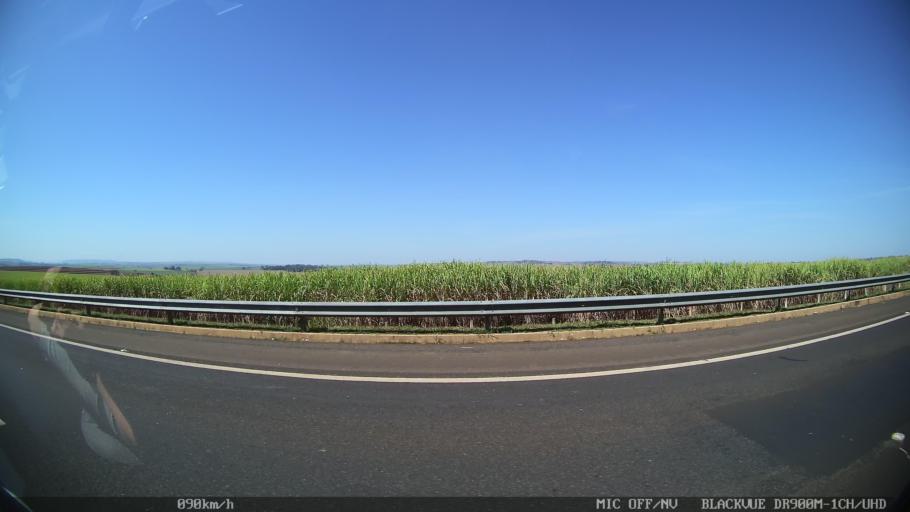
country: BR
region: Sao Paulo
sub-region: Batatais
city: Batatais
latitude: -20.7678
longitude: -47.5377
